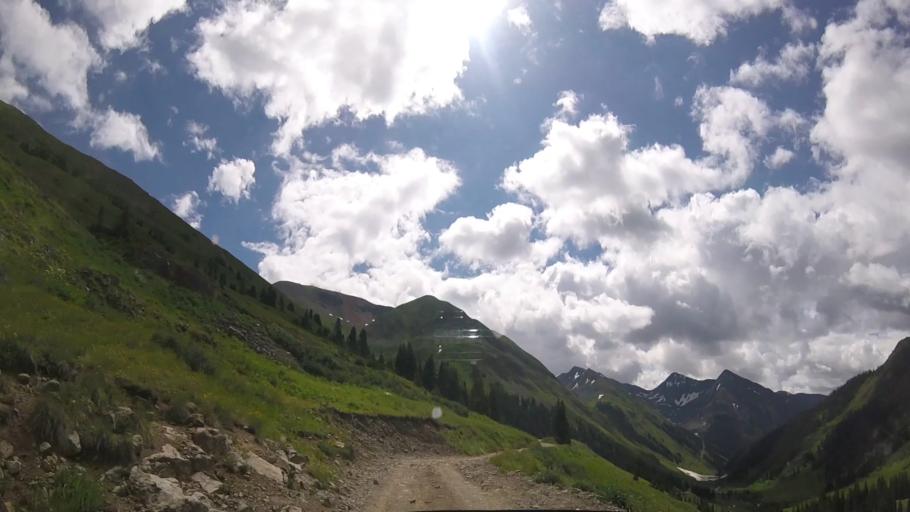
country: US
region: Colorado
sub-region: Ouray County
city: Ouray
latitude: 37.9308
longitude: -107.5673
